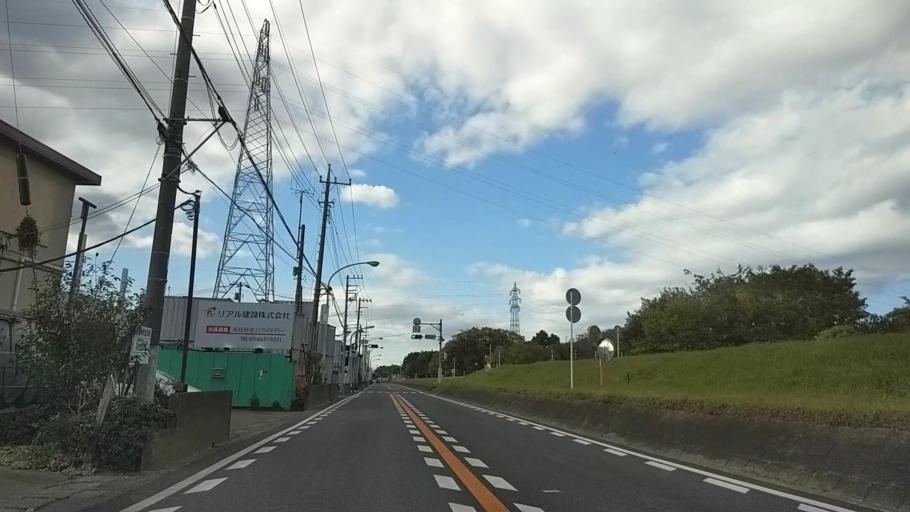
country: JP
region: Tokyo
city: Chofugaoka
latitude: 35.6143
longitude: 139.6047
